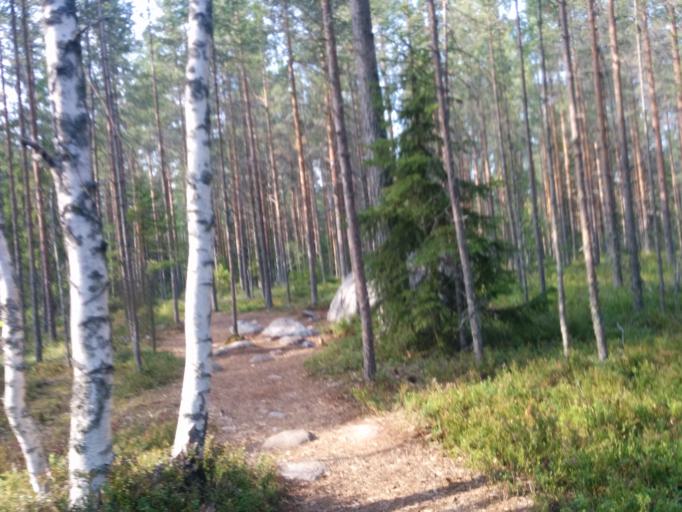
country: SE
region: Vaesterbotten
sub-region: Umea Kommun
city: Ersmark
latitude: 63.8184
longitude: 20.3611
